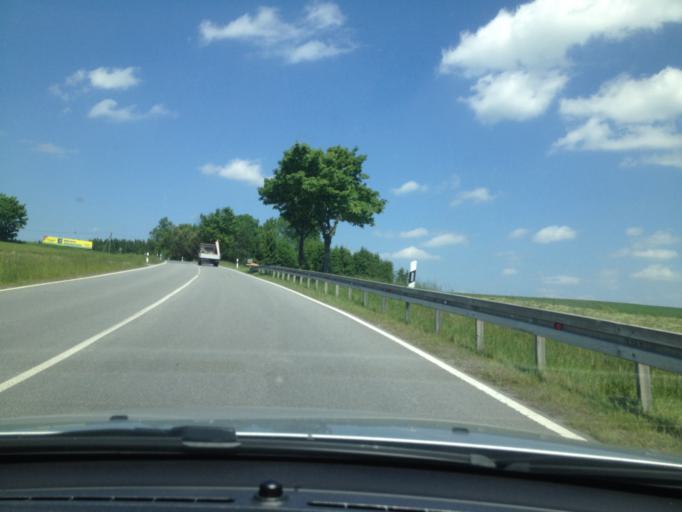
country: DE
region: Saxony
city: Thum
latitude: 50.6830
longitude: 12.9424
